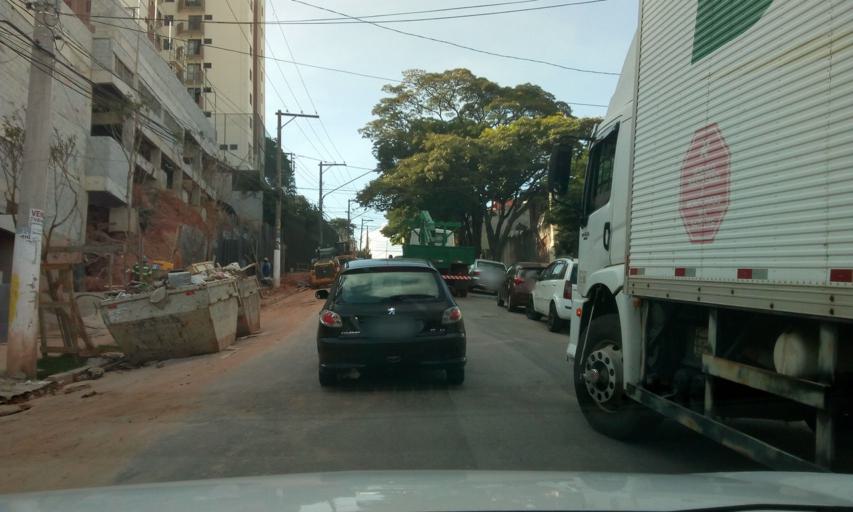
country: BR
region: Sao Paulo
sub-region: Sao Paulo
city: Sao Paulo
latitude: -23.4994
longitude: -46.6797
